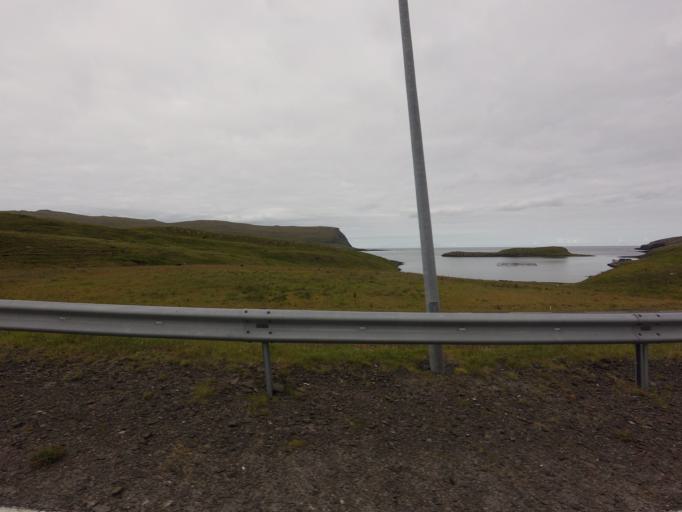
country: FO
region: Suduroy
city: Tvoroyri
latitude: 61.5301
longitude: -6.7963
